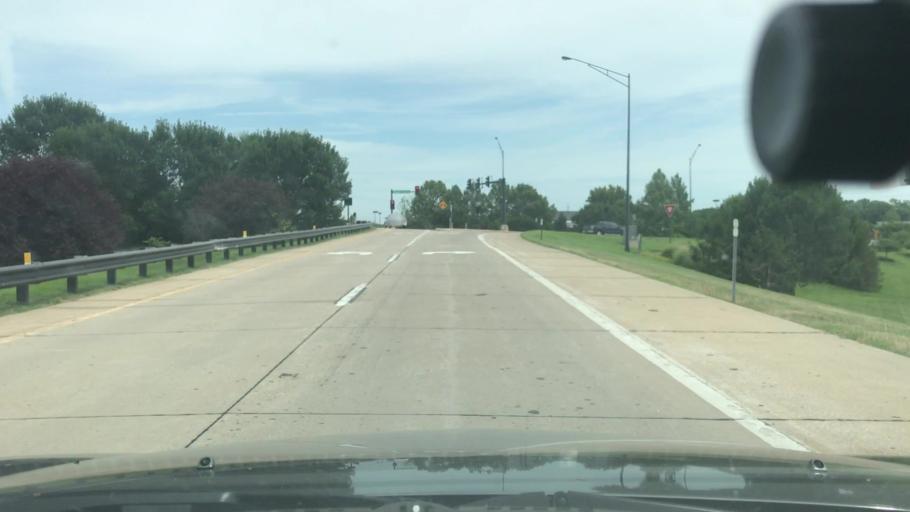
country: US
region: Missouri
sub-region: Saint Louis County
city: Chesterfield
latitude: 38.6700
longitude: -90.6009
